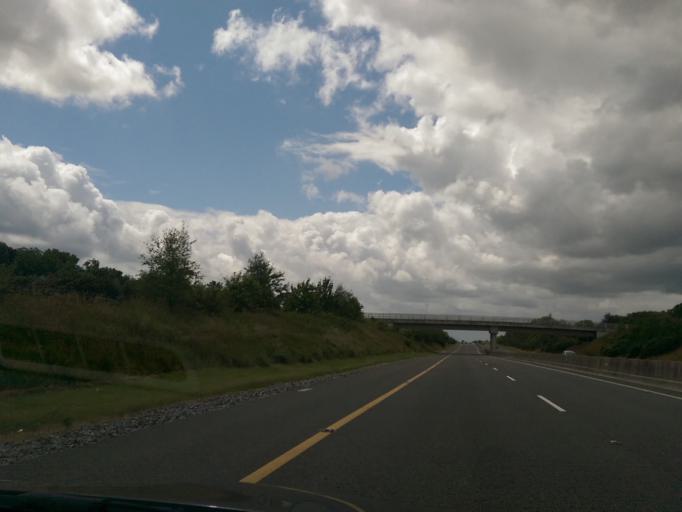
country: IE
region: Munster
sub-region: County Cork
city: Mitchelstown
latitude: 52.3095
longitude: -8.1511
